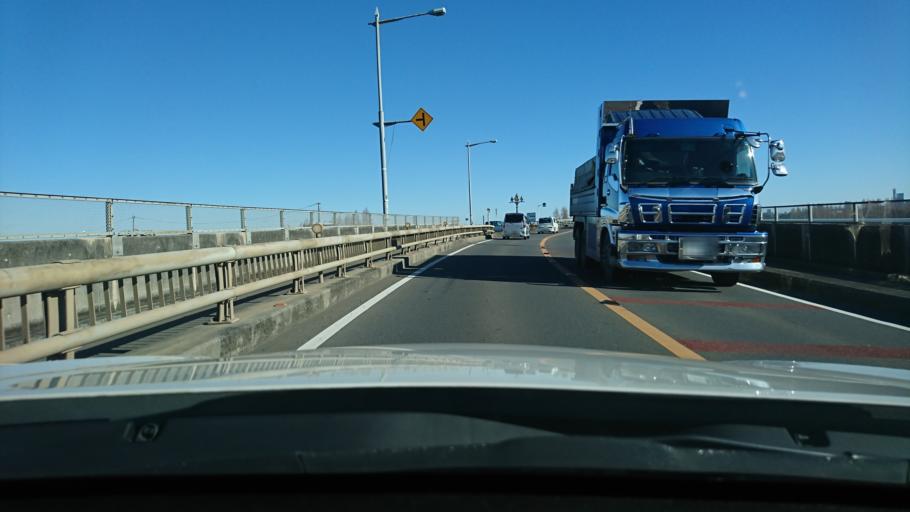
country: JP
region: Saitama
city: Kamifukuoka
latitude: 35.8913
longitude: 139.5589
